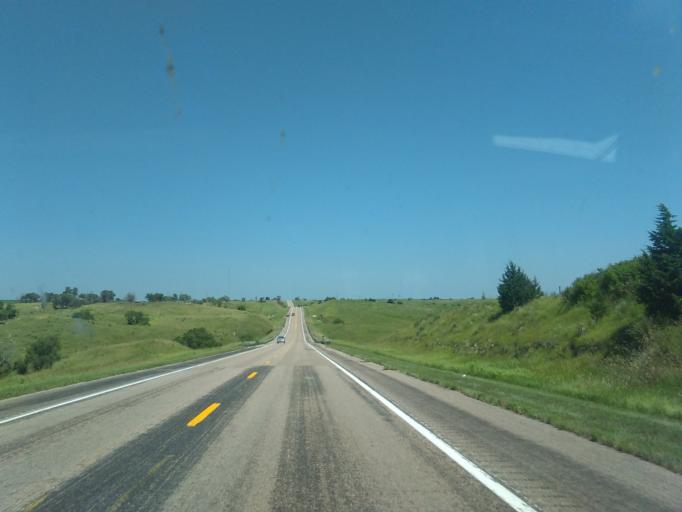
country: US
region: Nebraska
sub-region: Frontier County
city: Stockville
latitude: 40.5829
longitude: -100.6296
